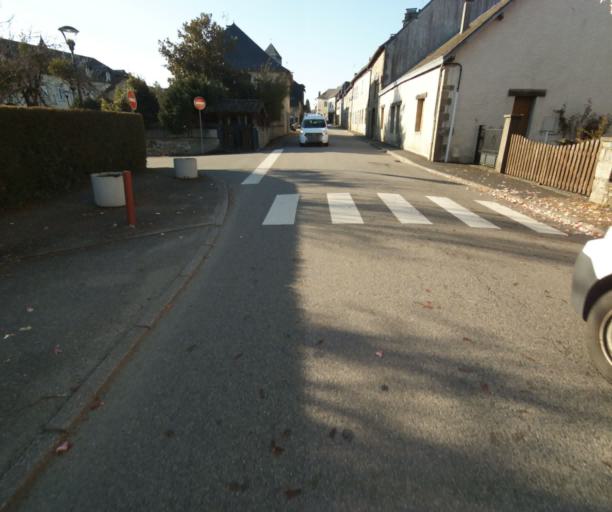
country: FR
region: Limousin
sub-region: Departement de la Correze
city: Chamboulive
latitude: 45.4311
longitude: 1.7054
